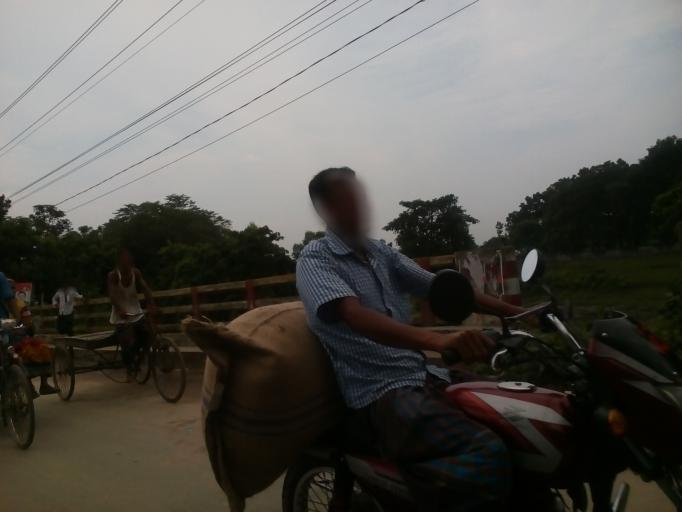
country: BD
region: Rangpur Division
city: Badarganj
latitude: 25.6685
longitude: 89.0505
